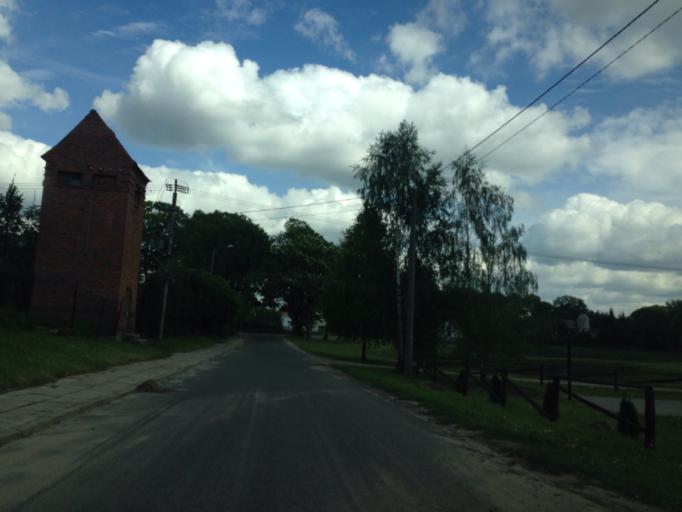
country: PL
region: Warmian-Masurian Voivodeship
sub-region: Powiat nidzicki
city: Nidzica
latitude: 53.4401
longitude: 20.3307
